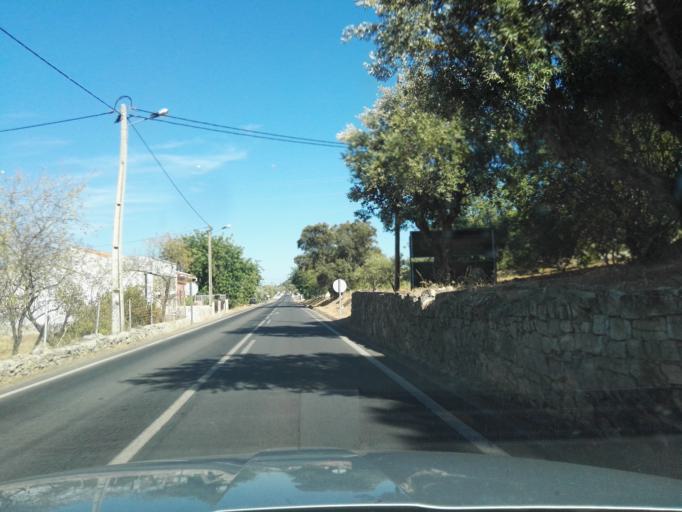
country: PT
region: Faro
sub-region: Sao Bras de Alportel
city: Sao Bras de Alportel
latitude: 37.1545
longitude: -7.8636
